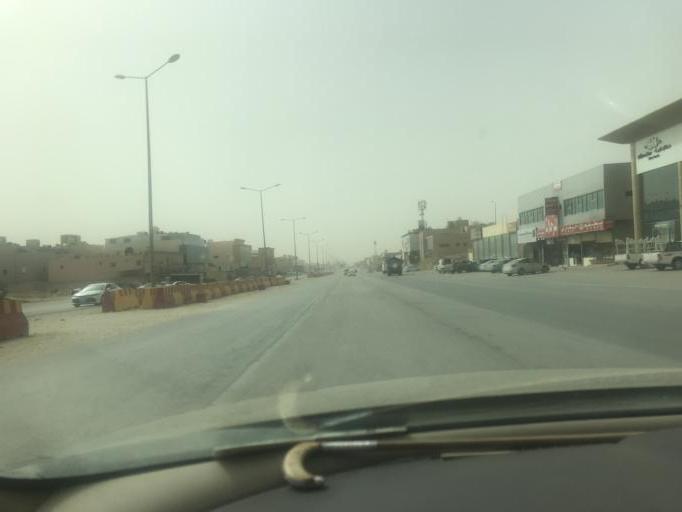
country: SA
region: Ar Riyad
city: Riyadh
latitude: 24.8096
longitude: 46.6008
